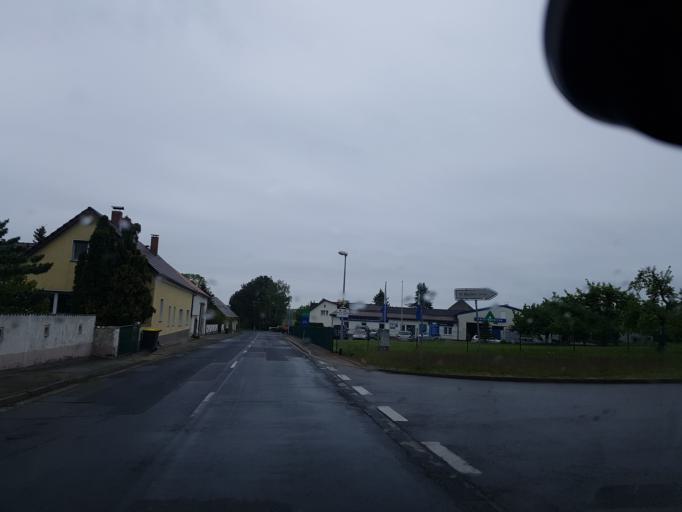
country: DE
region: Brandenburg
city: Cottbus
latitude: 51.6777
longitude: 14.3621
